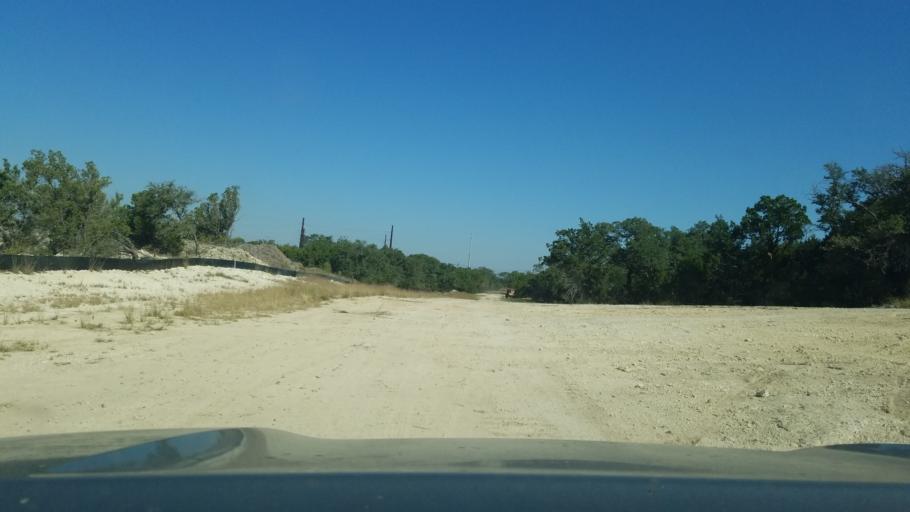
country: US
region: Texas
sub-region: Kendall County
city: Boerne
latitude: 29.7583
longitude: -98.7196
